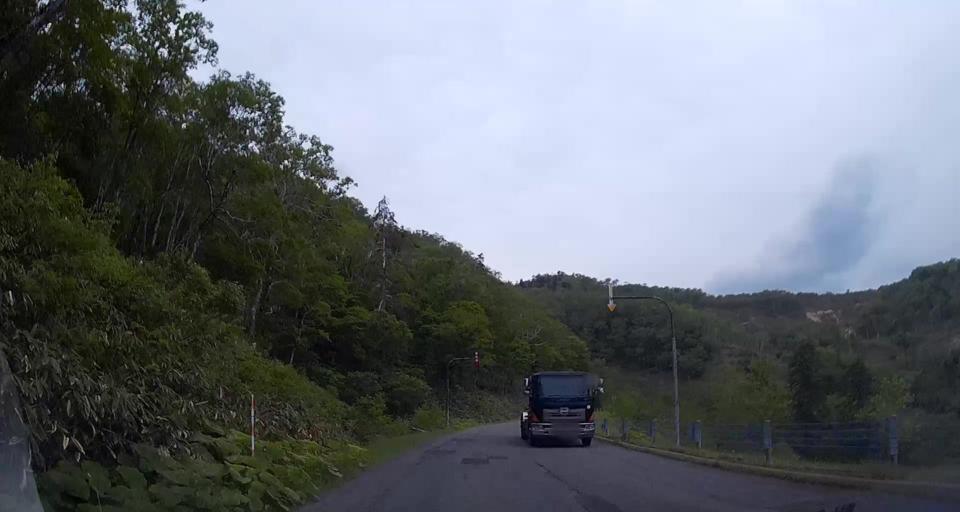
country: JP
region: Hokkaido
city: Shiraoi
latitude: 42.6604
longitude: 141.1681
